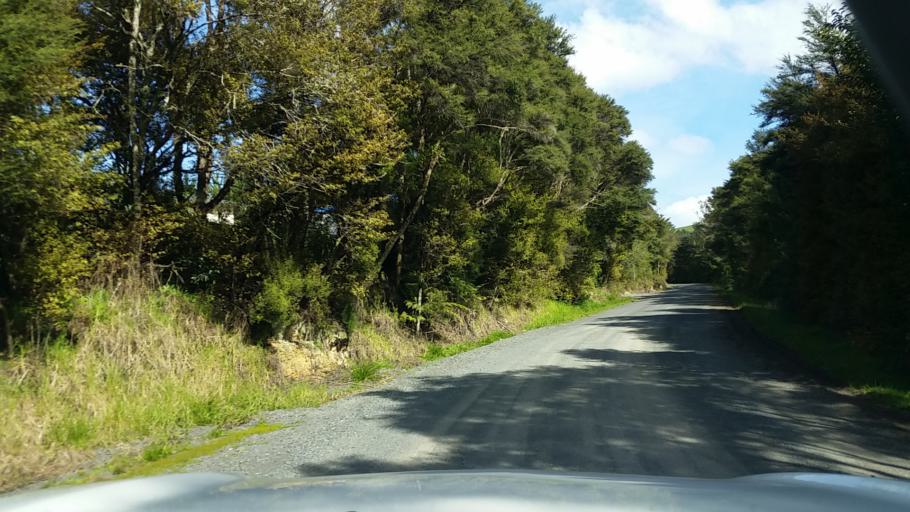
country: NZ
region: Waikato
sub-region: Hauraki District
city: Ngatea
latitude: -37.4496
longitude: 175.4748
